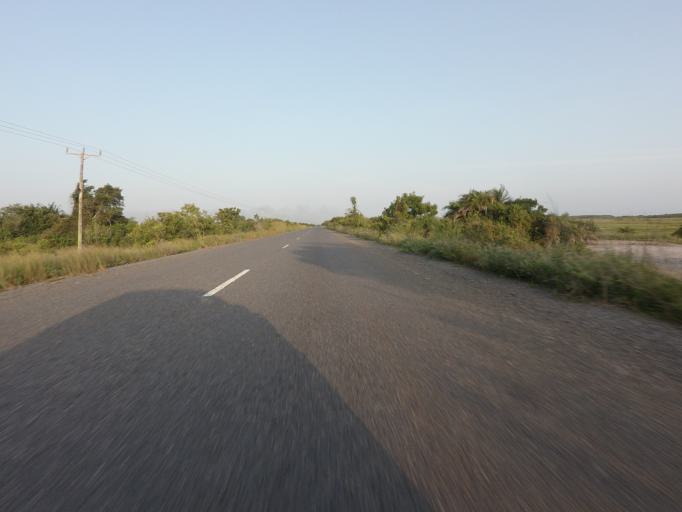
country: GH
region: Volta
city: Anloga
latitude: 5.8506
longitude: 0.7736
